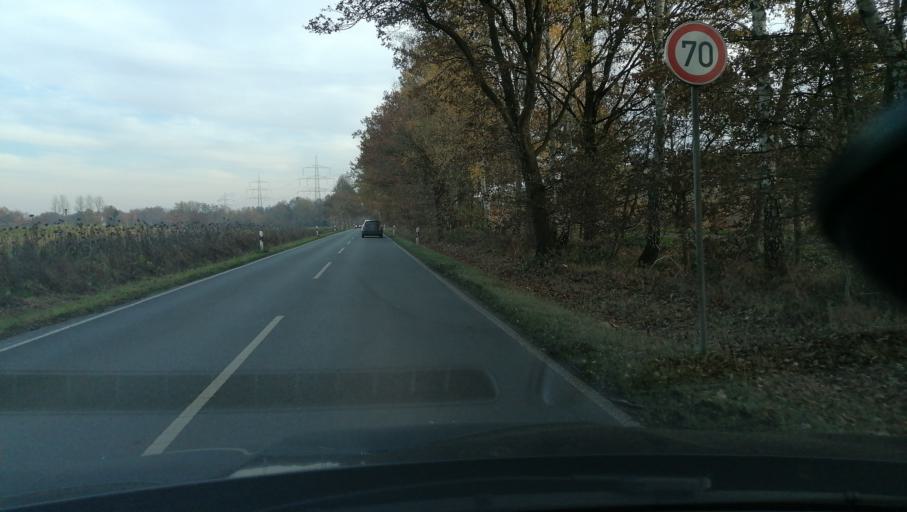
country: DE
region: North Rhine-Westphalia
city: Castrop-Rauxel
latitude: 51.5804
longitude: 7.2771
